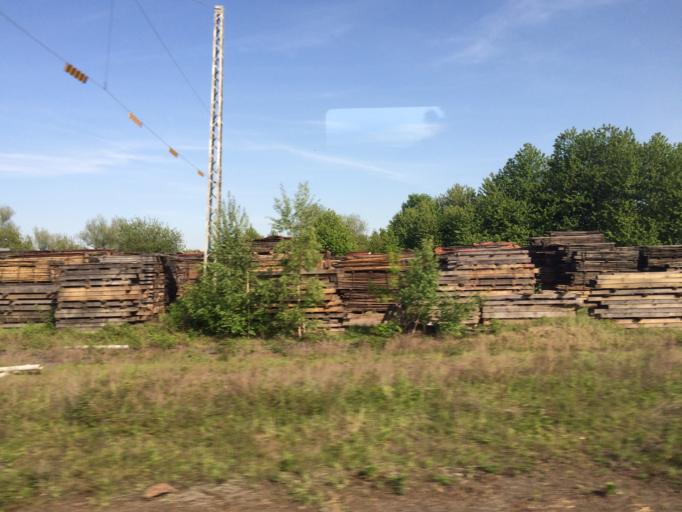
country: DE
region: North Rhine-Westphalia
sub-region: Regierungsbezirk Koln
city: Troisdorf
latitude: 50.7741
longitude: 7.1461
